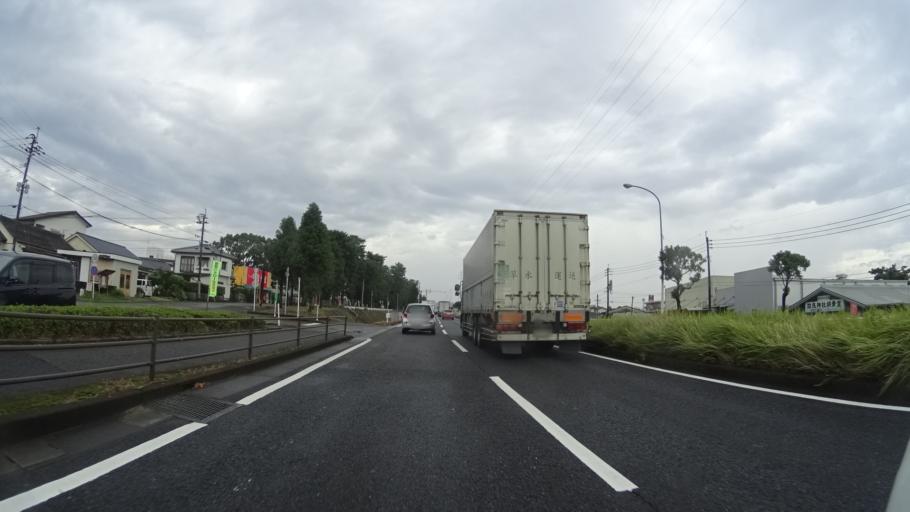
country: JP
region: Kagoshima
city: Kajiki
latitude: 31.7116
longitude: 130.6165
